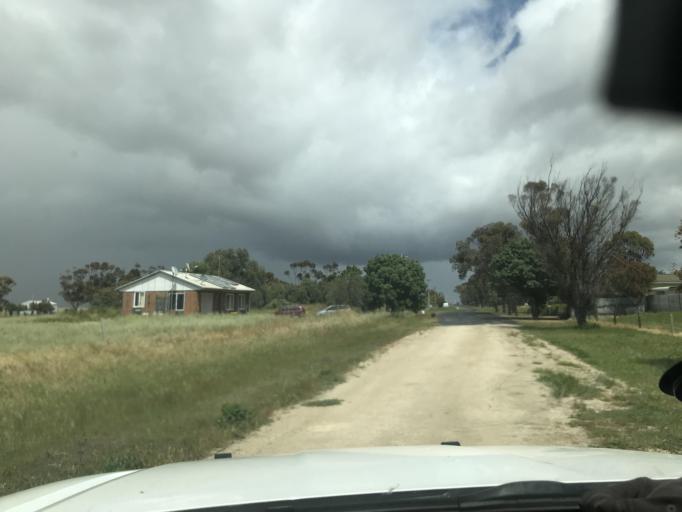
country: AU
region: South Australia
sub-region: Tatiara
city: Bordertown
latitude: -36.3764
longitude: 140.9913
